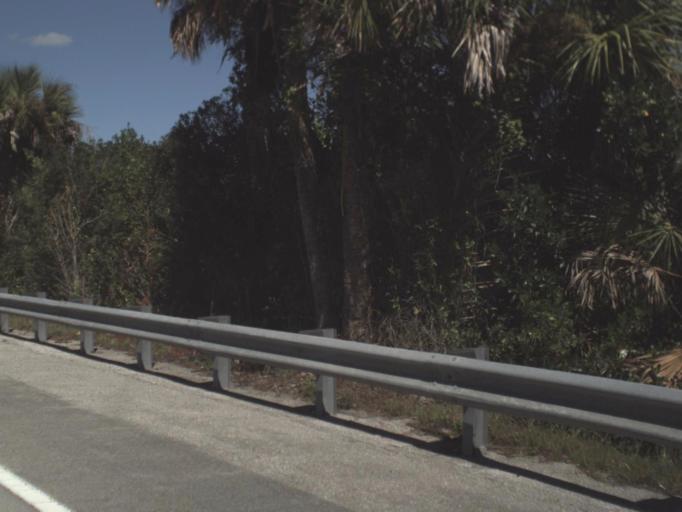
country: US
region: Florida
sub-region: Collier County
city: Marco
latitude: 25.9810
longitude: -81.5620
